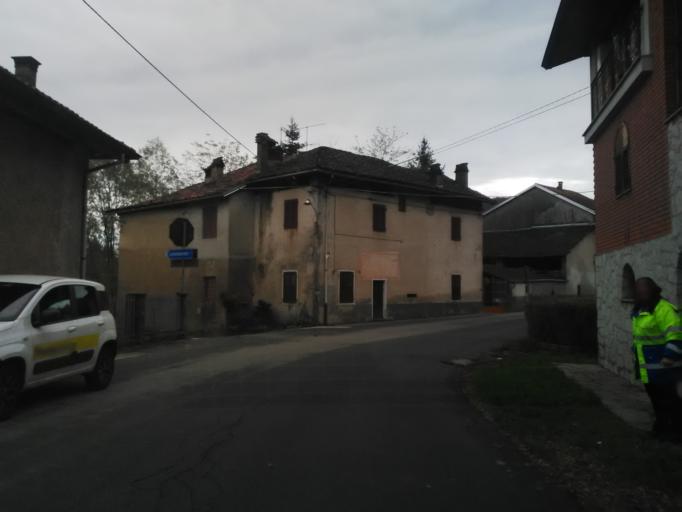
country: IT
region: Piedmont
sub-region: Provincia di Vercelli
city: Guardabosone
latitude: 45.6957
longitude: 8.2467
